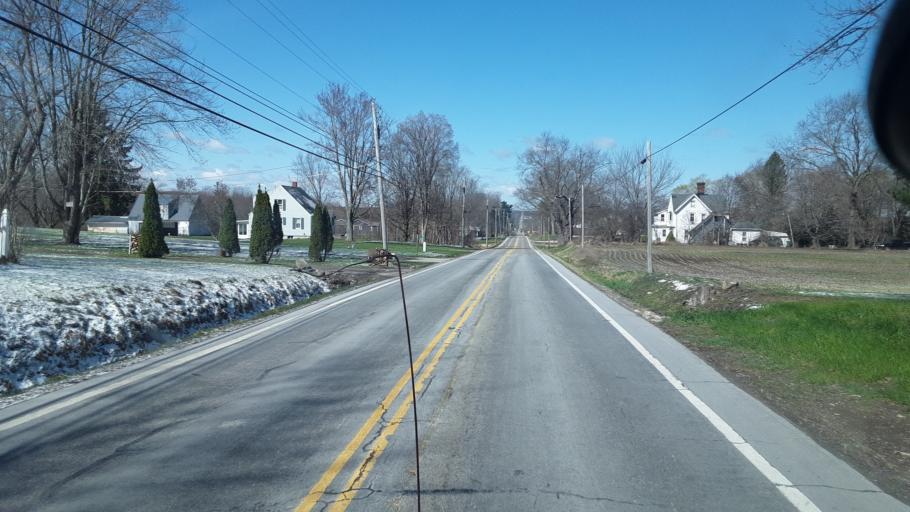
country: US
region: Ohio
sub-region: Ashtabula County
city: Andover
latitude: 41.6070
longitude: -80.6048
